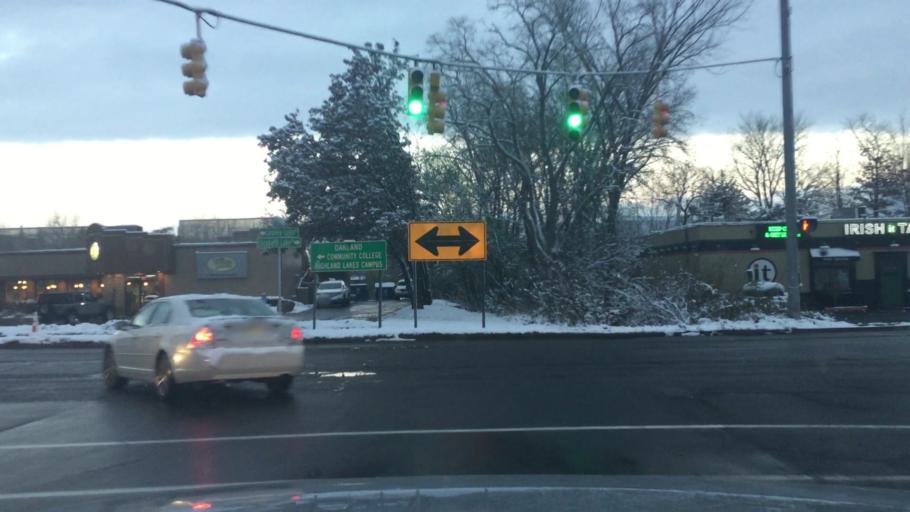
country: US
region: Michigan
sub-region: Oakland County
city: Keego Harbor
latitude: 42.6386
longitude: -83.3815
